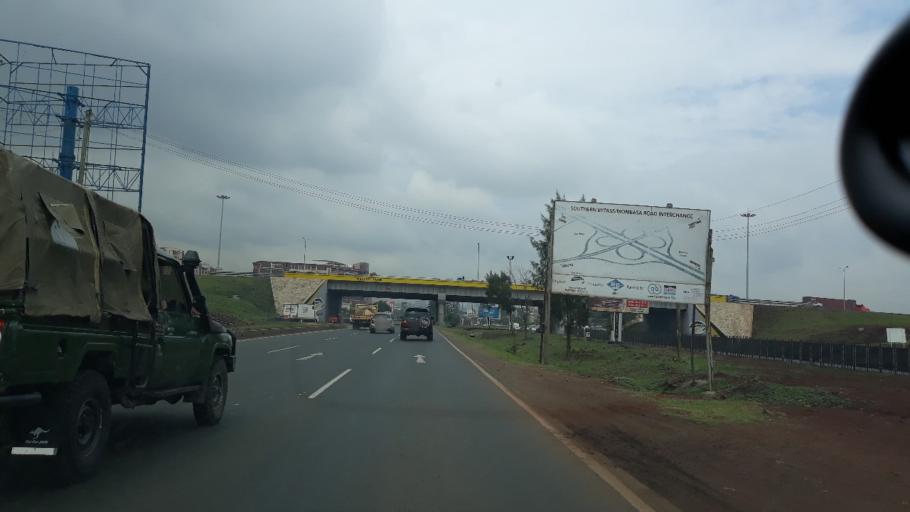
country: KE
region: Nairobi Area
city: Pumwani
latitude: -1.3257
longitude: 36.8483
